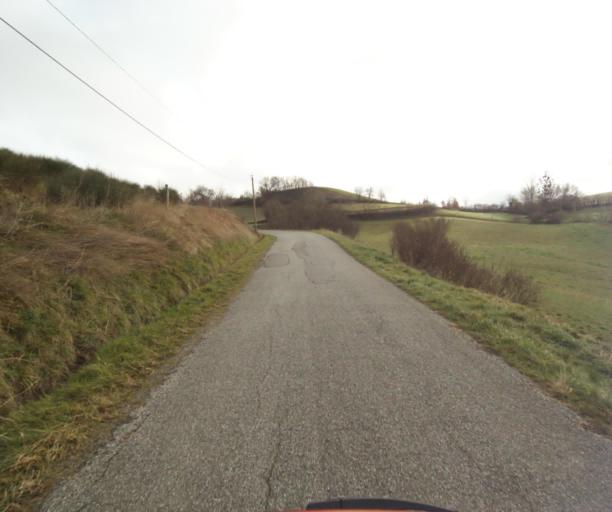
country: FR
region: Midi-Pyrenees
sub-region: Departement de la Haute-Garonne
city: Gaillac-Toulza
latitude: 43.1697
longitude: 1.5052
